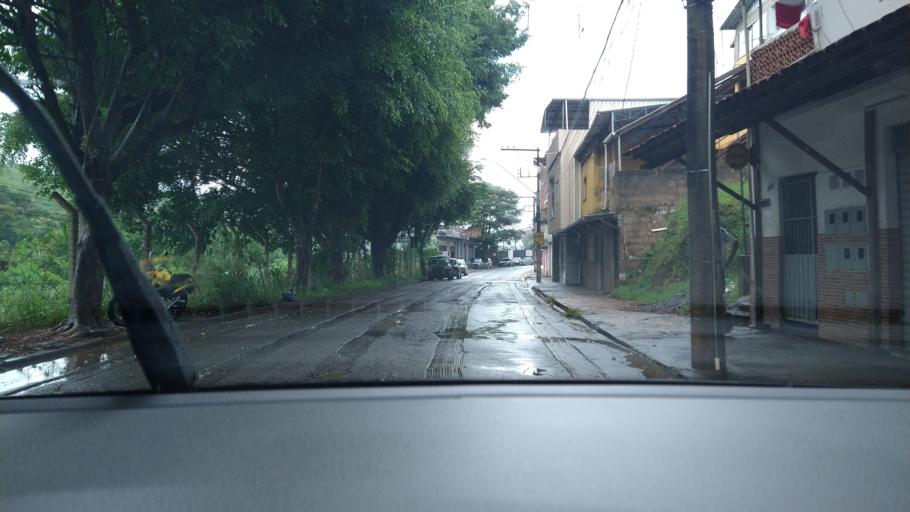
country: BR
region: Minas Gerais
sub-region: Ponte Nova
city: Ponte Nova
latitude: -20.4011
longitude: -42.9009
